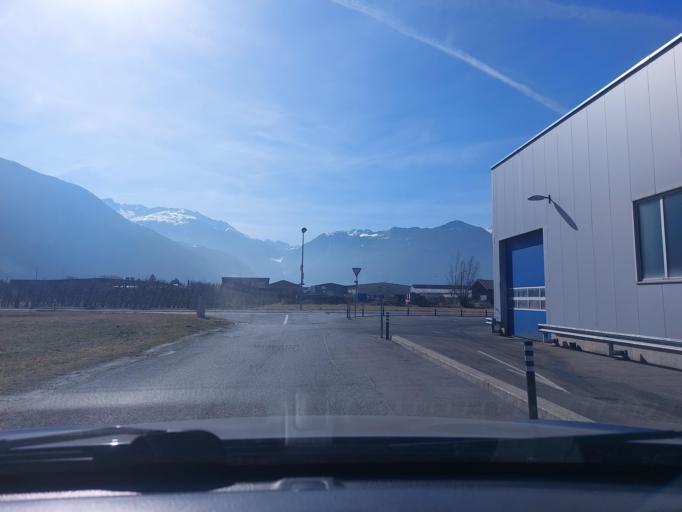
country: CH
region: Valais
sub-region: Martigny District
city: Charrat-les-Chenes
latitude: 46.1286
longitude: 7.1345
